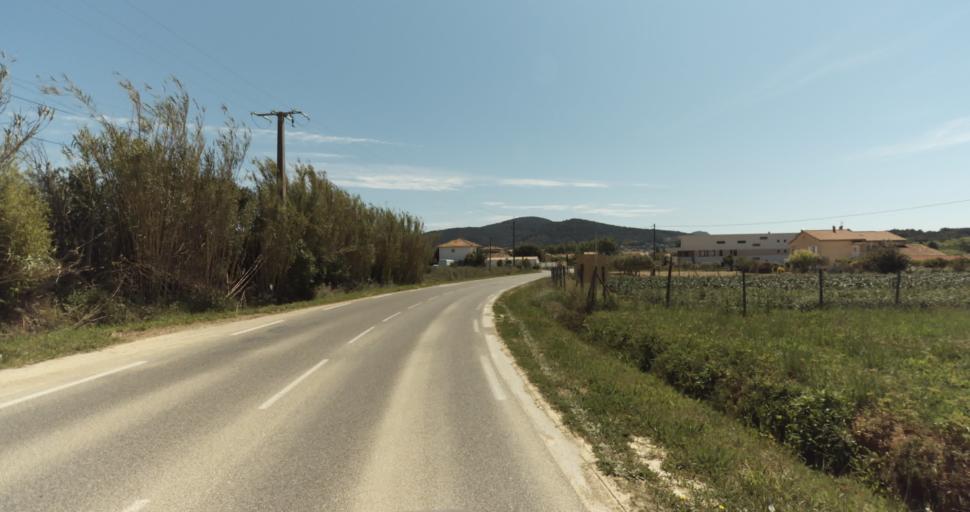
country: FR
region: Provence-Alpes-Cote d'Azur
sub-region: Departement du Var
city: La Crau
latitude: 43.1327
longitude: 6.0779
